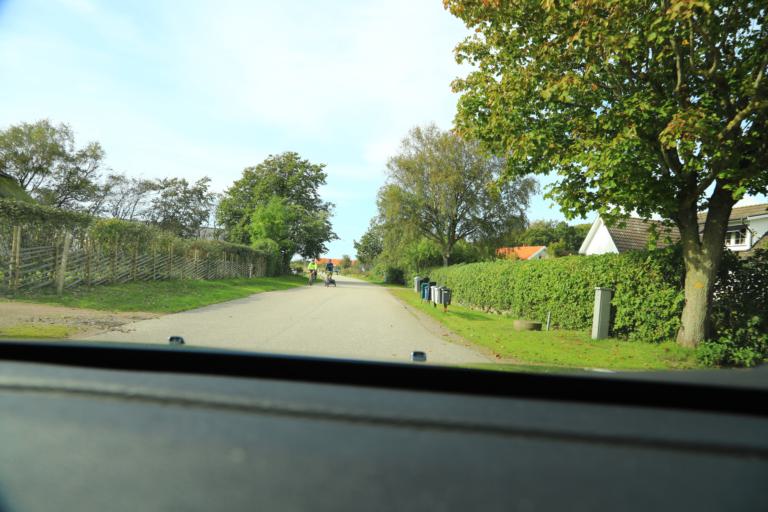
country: SE
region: Halland
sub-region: Varbergs Kommun
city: Traslovslage
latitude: 57.0414
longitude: 12.3194
